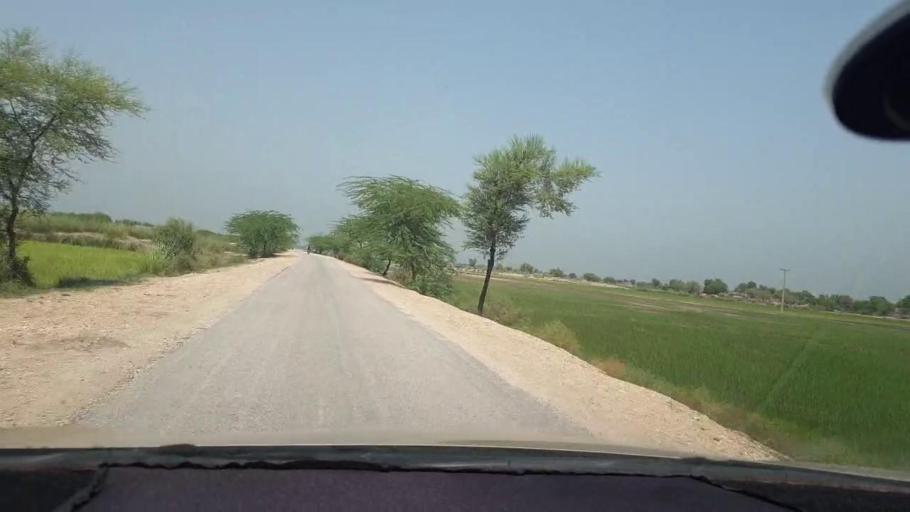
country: PK
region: Sindh
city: Kambar
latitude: 27.6723
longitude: 67.9122
